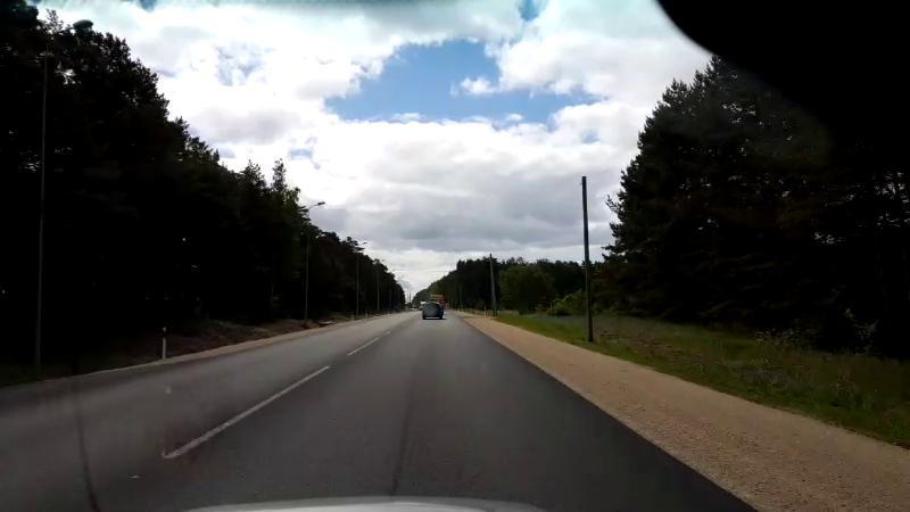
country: LV
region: Salacgrivas
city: Salacgriva
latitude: 57.7789
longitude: 24.3547
